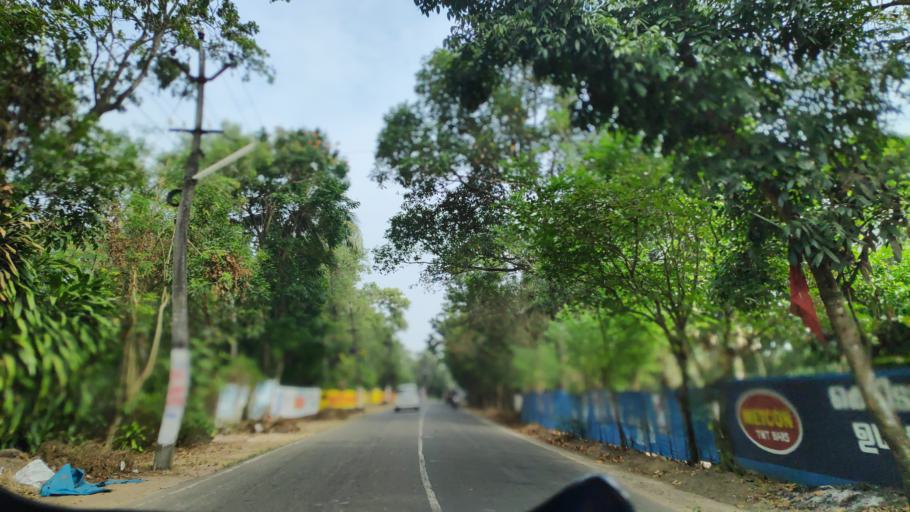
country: IN
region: Kerala
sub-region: Kottayam
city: Vaikam
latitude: 9.7696
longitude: 76.3625
